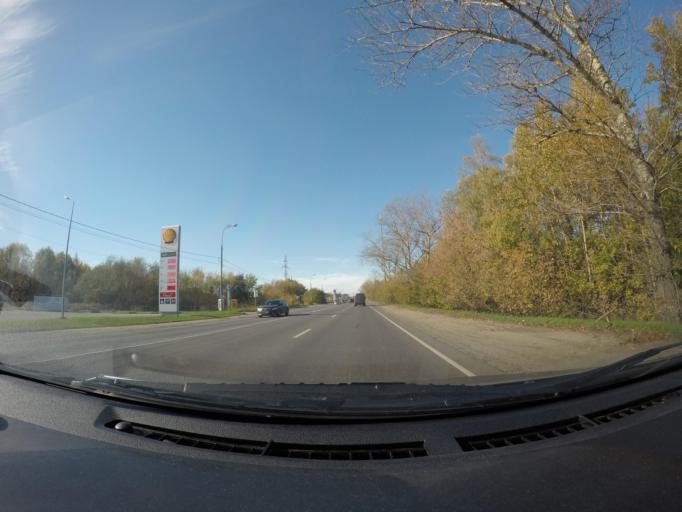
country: RU
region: Moskovskaya
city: Tomilino
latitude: 55.6336
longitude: 37.9609
